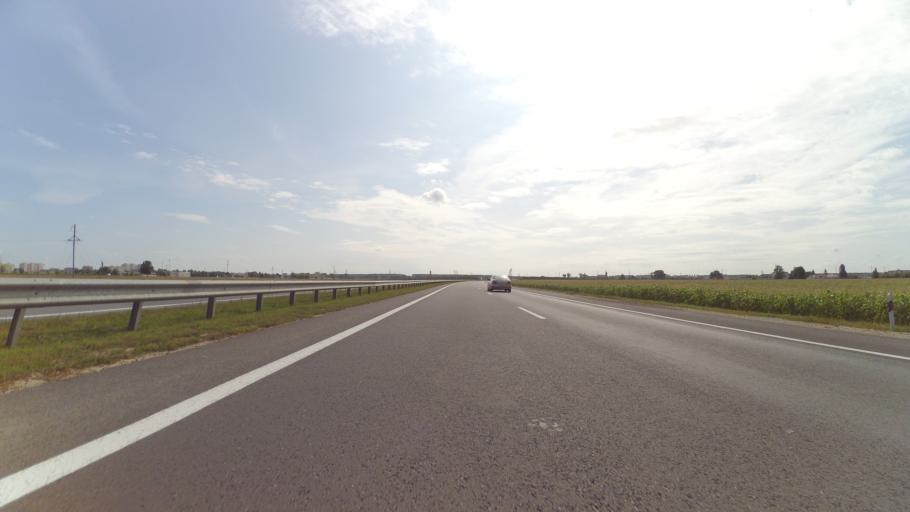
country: BY
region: Grodnenskaya
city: Skidal'
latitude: 53.5832
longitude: 24.2213
